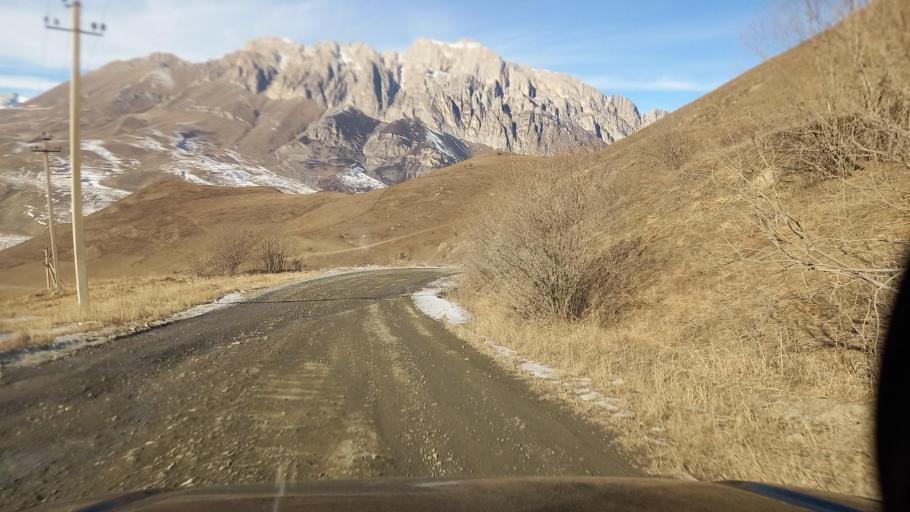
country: RU
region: North Ossetia
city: Verkhniy Fiagdon
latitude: 42.8372
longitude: 44.4675
